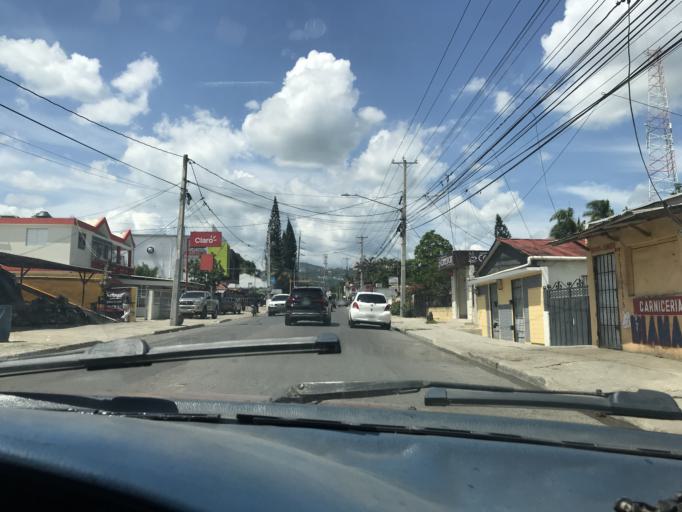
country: DO
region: Santiago
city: Tamboril
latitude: 19.4849
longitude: -70.6597
